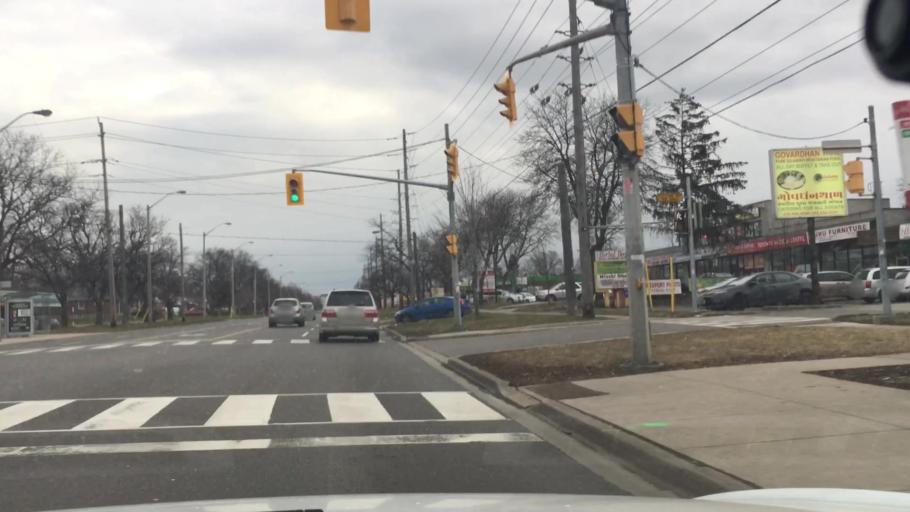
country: CA
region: Ontario
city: Scarborough
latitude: 43.7677
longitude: -79.2284
